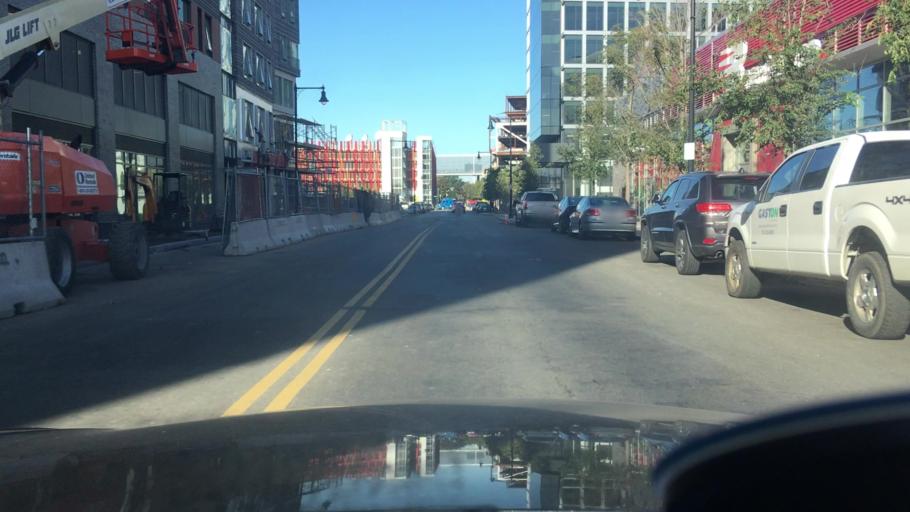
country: US
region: Massachusetts
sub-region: Norfolk County
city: Brookline
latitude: 42.3566
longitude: -71.1423
